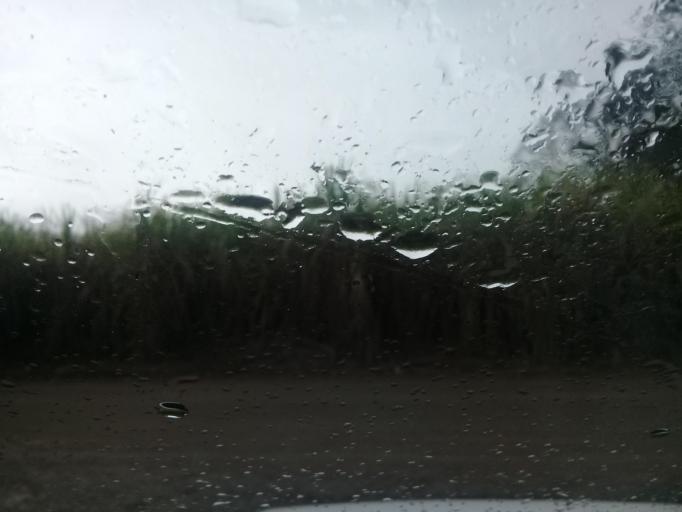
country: MX
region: Veracruz
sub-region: Amatlan de los Reyes
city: Centro de Readaptacion Social
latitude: 18.8427
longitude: -96.9407
